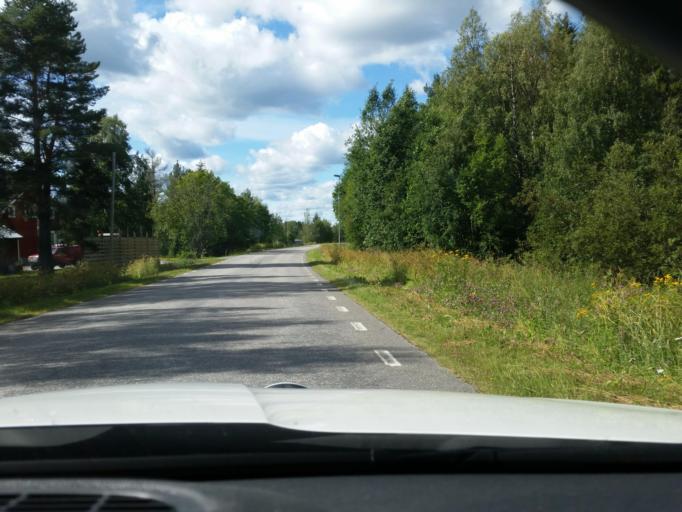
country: SE
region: Norrbotten
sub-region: Pitea Kommun
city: Norrfjarden
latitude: 65.5136
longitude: 21.3211
